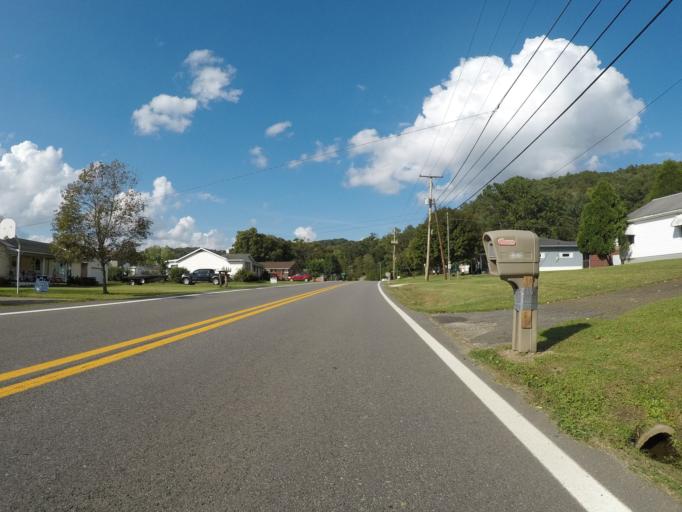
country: US
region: Ohio
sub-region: Lawrence County
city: Burlington
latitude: 38.3566
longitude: -82.5047
